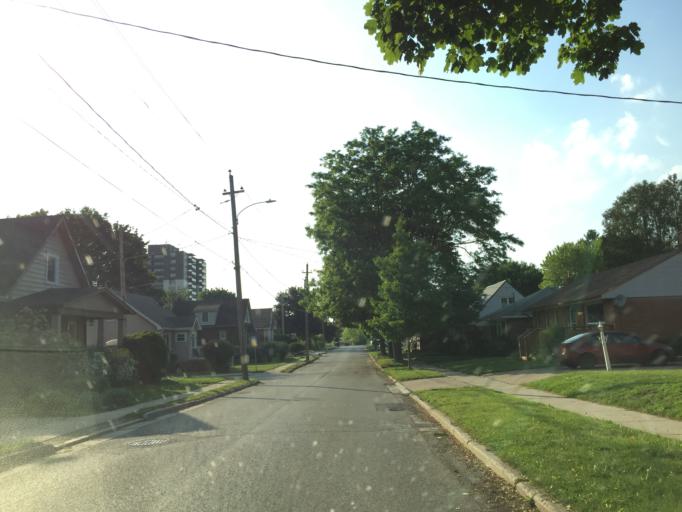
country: CA
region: Ontario
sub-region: Wellington County
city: Guelph
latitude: 43.5556
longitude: -80.2690
